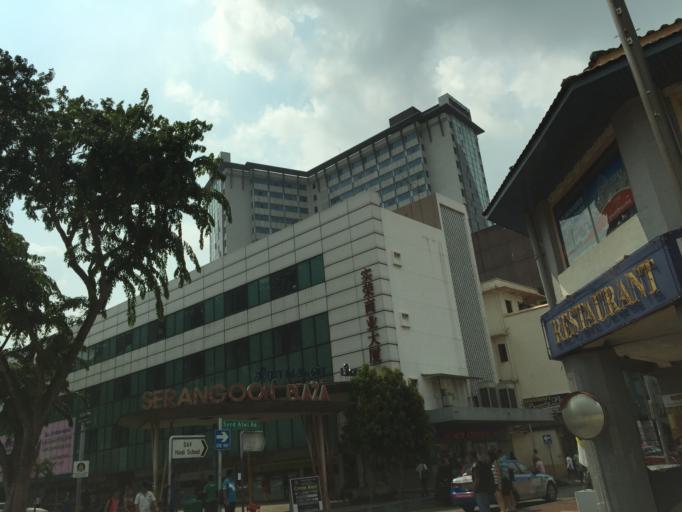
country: SG
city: Singapore
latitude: 1.3105
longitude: 103.8545
